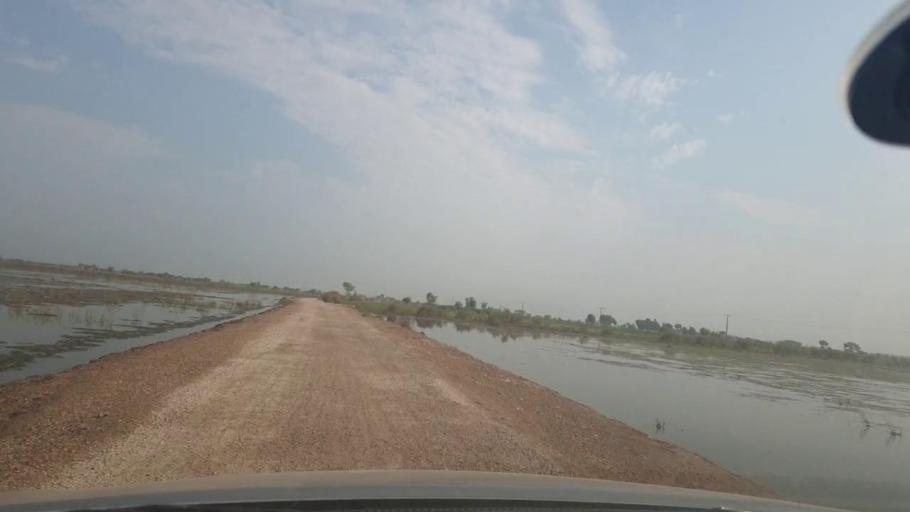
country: PK
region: Balochistan
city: Mehrabpur
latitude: 28.0639
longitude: 68.2100
